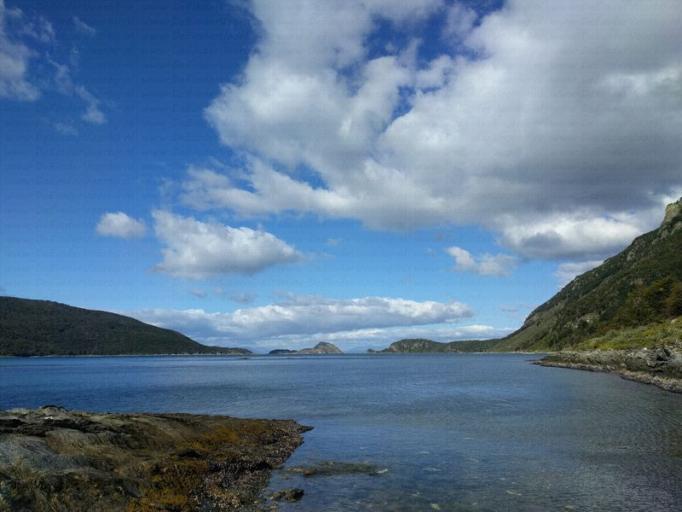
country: AR
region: Tierra del Fuego
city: Ushuaia
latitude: -54.8594
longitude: -68.5626
